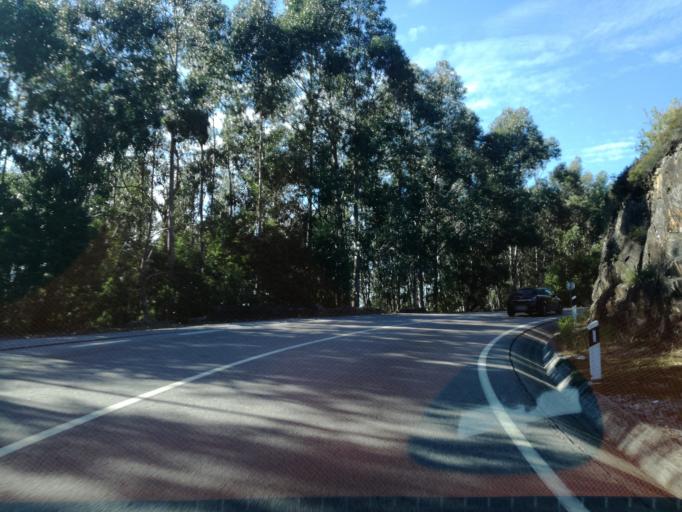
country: PT
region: Porto
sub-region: Pacos de Ferreira
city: Seroa
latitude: 41.2586
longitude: -8.4605
